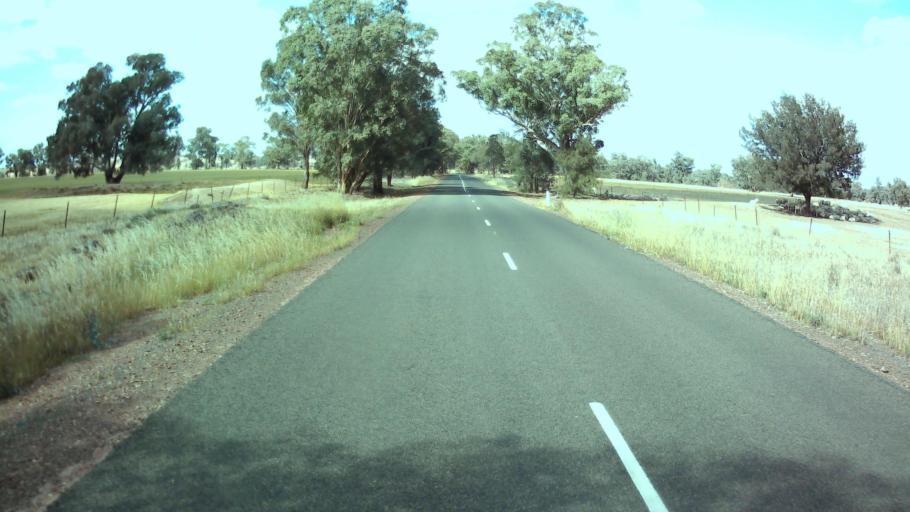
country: AU
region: New South Wales
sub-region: Weddin
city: Grenfell
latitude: -33.9825
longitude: 148.4171
